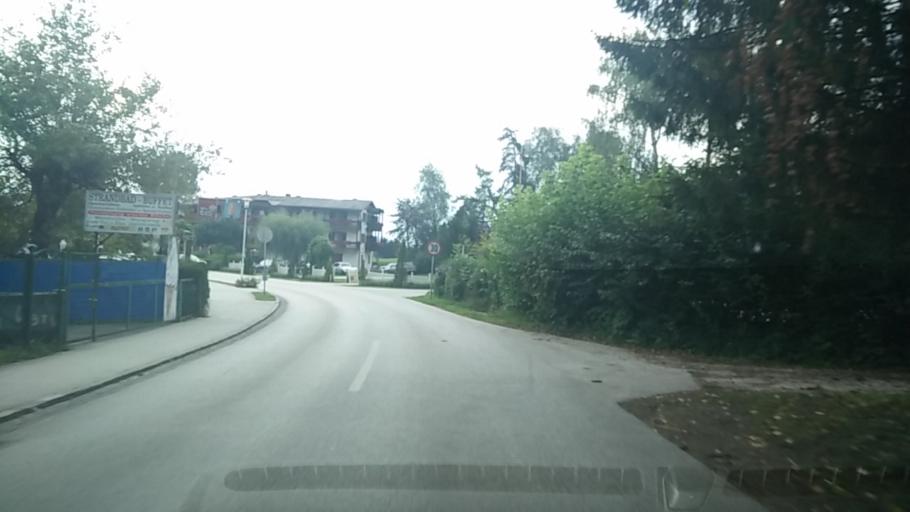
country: AT
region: Carinthia
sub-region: Politischer Bezirk Volkermarkt
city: Eberndorf
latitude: 46.6048
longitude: 14.5968
